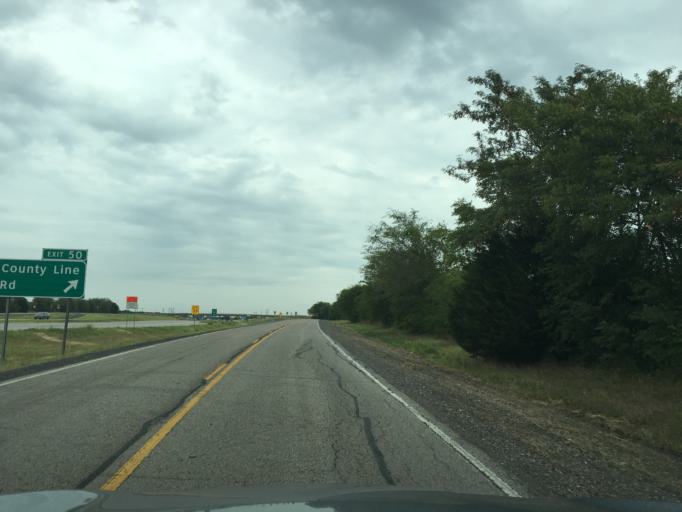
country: US
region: Texas
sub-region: Grayson County
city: Van Alstyne
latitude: 33.3956
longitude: -96.5800
